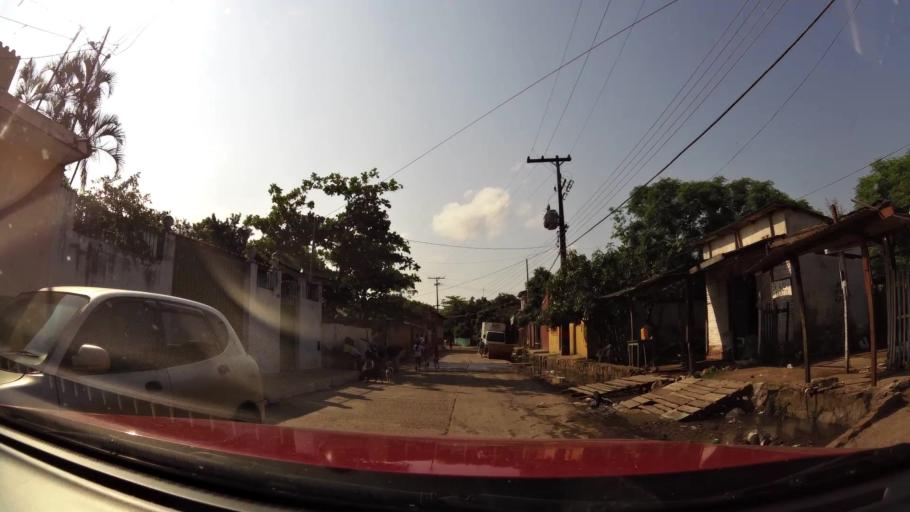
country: PY
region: Asuncion
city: Asuncion
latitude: -25.3216
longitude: -57.6429
